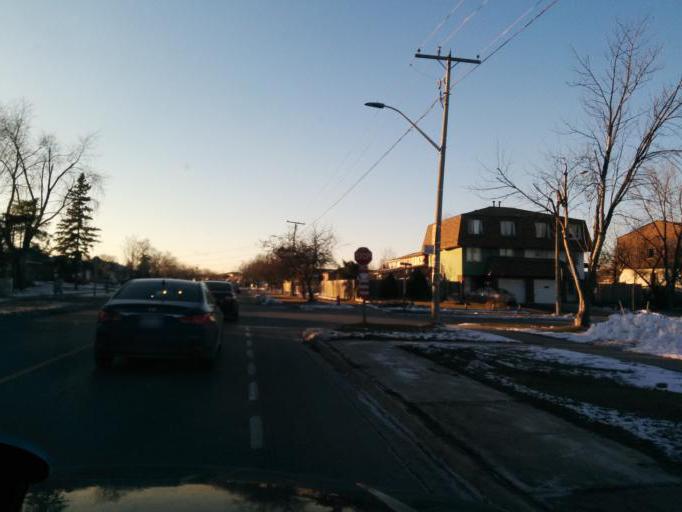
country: CA
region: Ontario
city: Etobicoke
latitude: 43.7253
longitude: -79.6271
